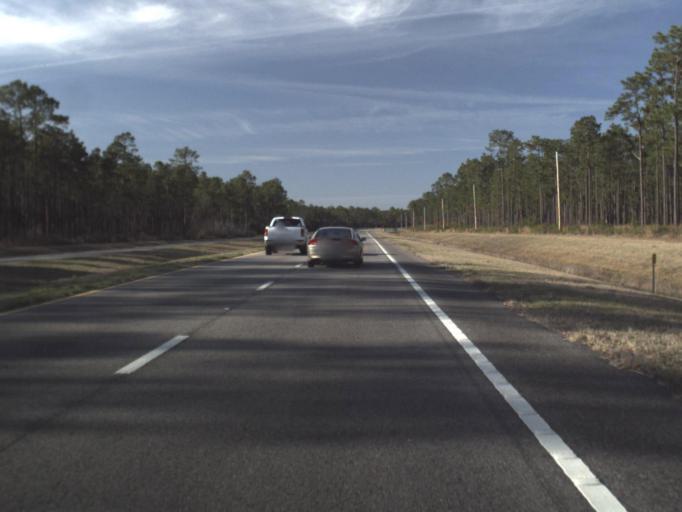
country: US
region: Florida
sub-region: Bay County
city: Laguna Beach
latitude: 30.3834
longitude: -85.8690
